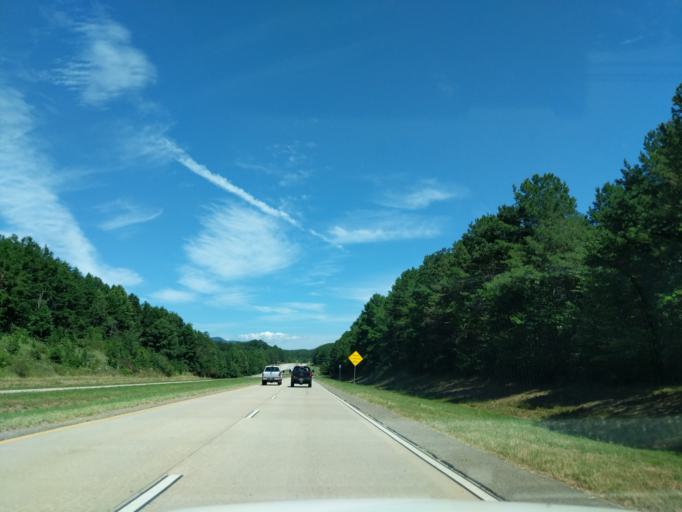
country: US
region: Georgia
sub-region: Union County
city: Blairsville
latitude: 34.8628
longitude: -83.9960
